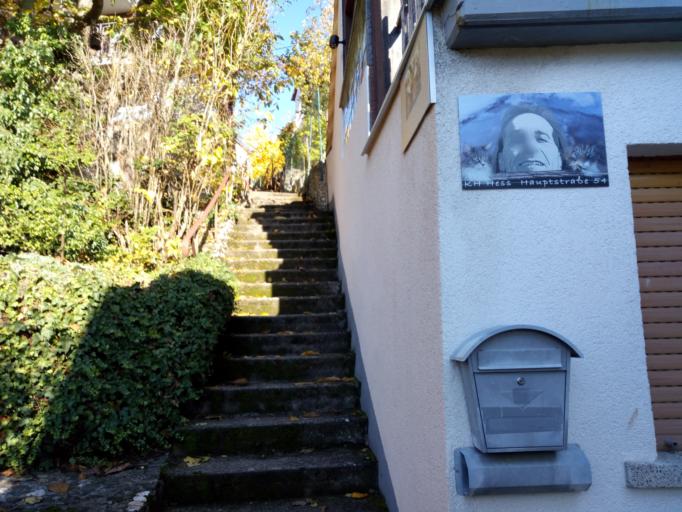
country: DE
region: Rheinland-Pfalz
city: Monzingen
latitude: 49.7987
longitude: 7.5914
